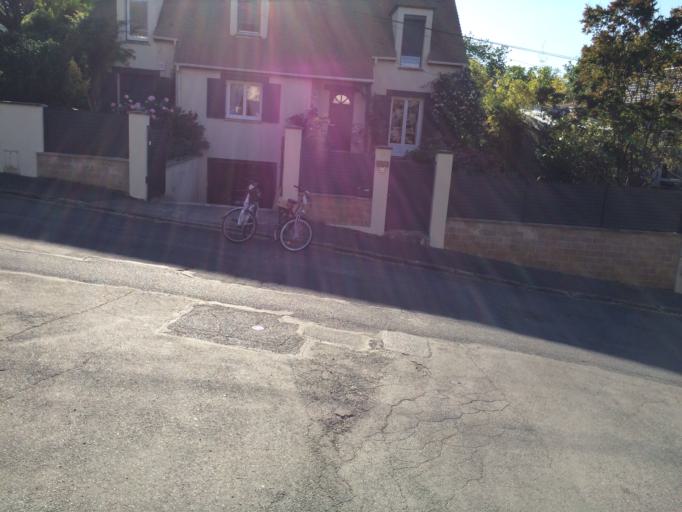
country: FR
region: Ile-de-France
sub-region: Departement de l'Essonne
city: Igny
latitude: 48.7287
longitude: 2.2198
